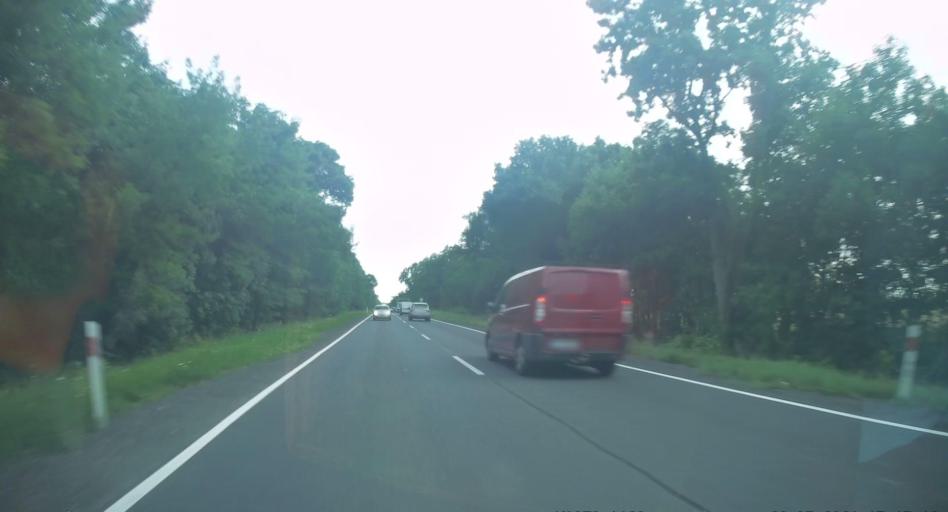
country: PL
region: Lodz Voivodeship
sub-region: Powiat radomszczanski
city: Plawno
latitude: 50.9704
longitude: 19.4077
